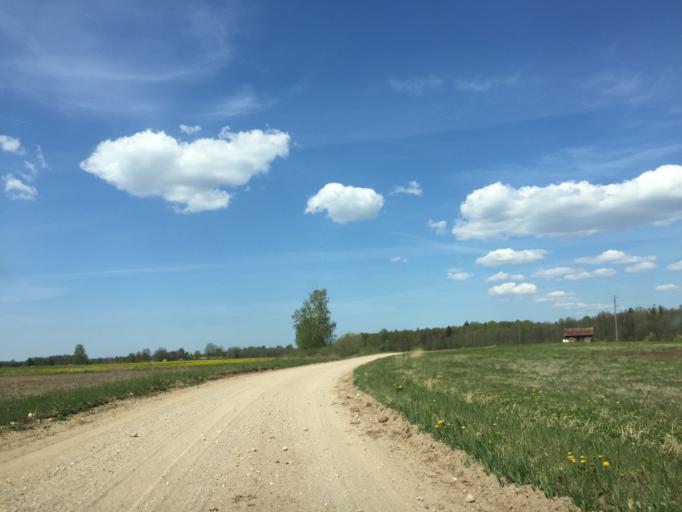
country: LV
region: Limbazu Rajons
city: Limbazi
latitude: 57.3762
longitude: 24.6283
